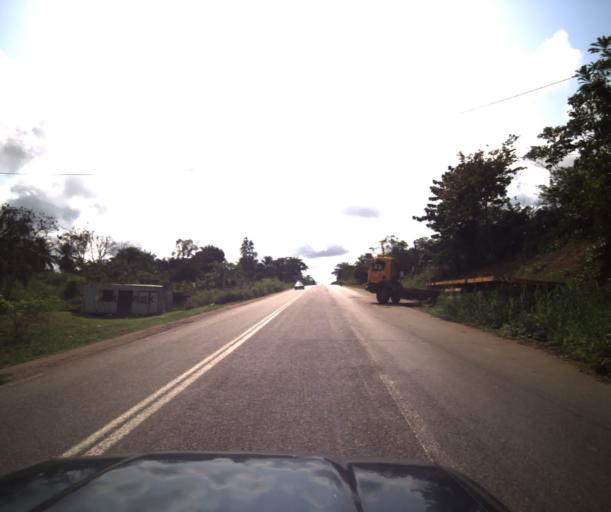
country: CM
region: Littoral
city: Edea
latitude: 3.7853
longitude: 10.1508
